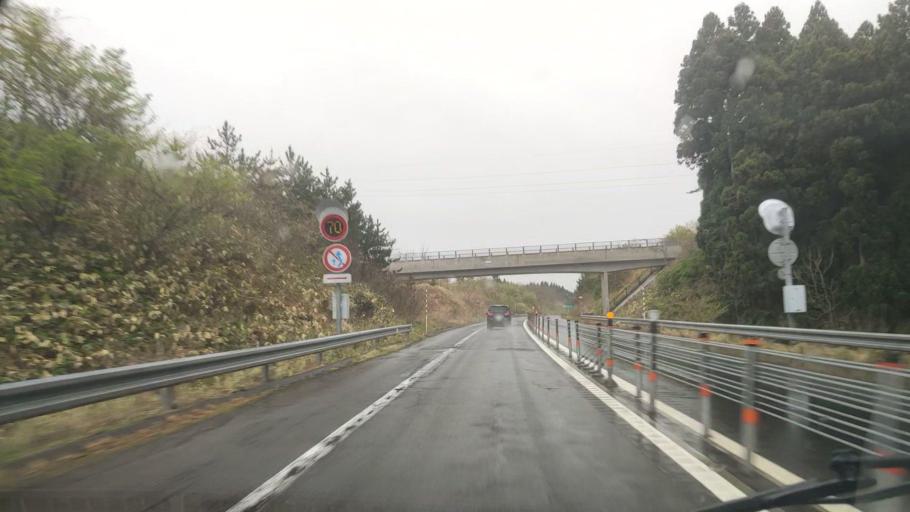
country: JP
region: Akita
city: Noshiromachi
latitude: 40.1655
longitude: 140.0480
